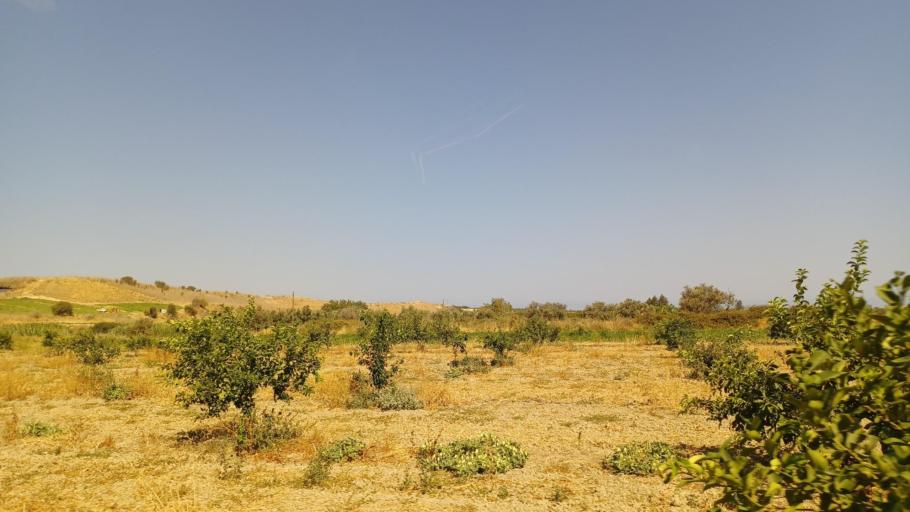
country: CY
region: Pafos
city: Polis
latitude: 35.0108
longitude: 32.4321
